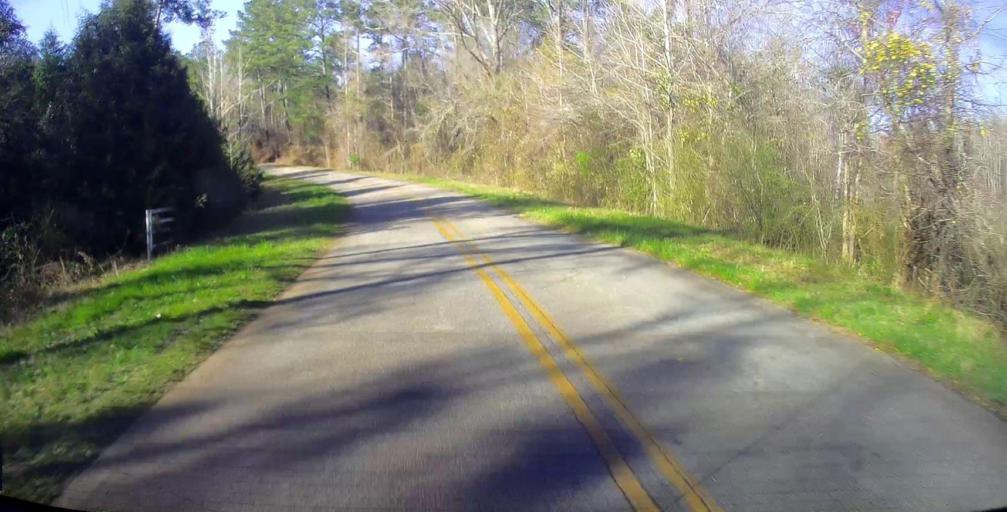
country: US
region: Georgia
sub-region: Macon County
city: Marshallville
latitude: 32.4747
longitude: -83.9511
